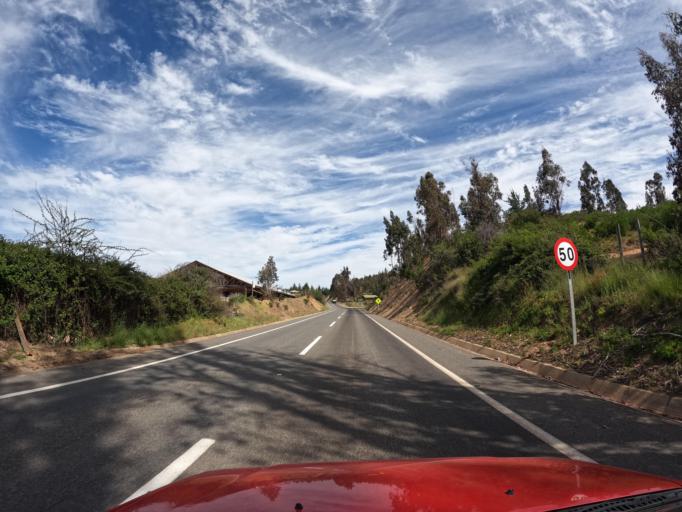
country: CL
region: Maule
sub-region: Provincia de Talca
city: Talca
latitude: -35.1490
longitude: -71.9634
